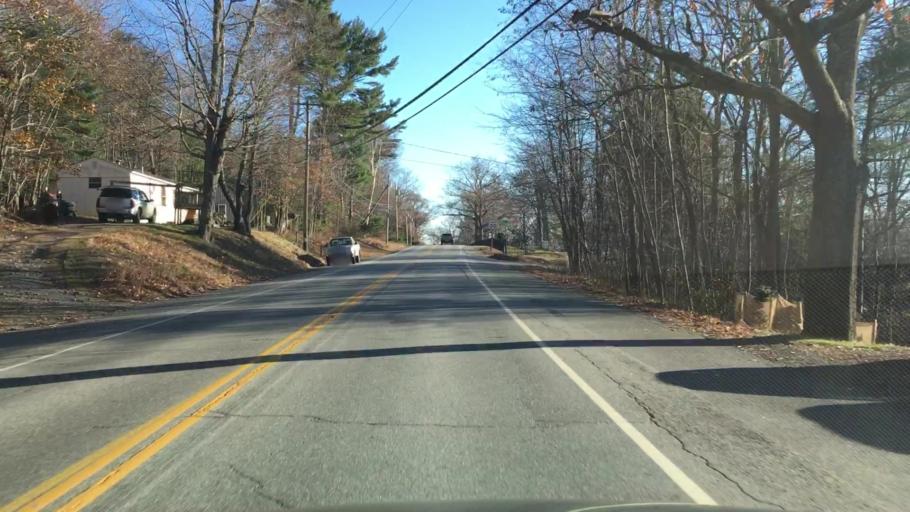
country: US
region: Maine
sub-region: Knox County
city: Camden
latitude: 44.2201
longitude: -69.0744
